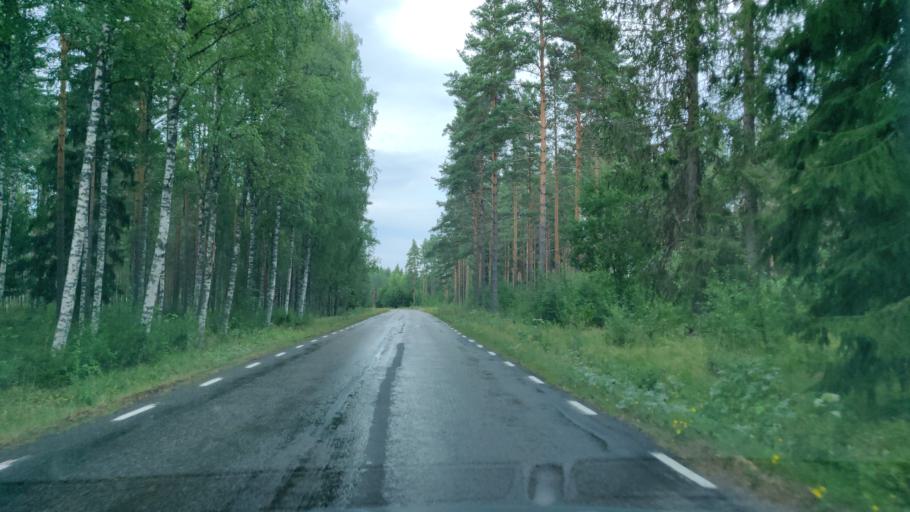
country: SE
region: Vaermland
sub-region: Munkfors Kommun
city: Munkfors
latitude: 59.8834
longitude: 13.5223
